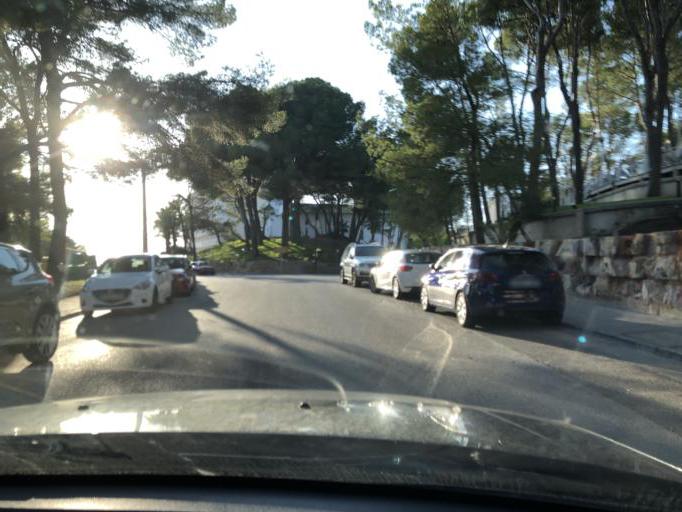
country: ES
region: Balearic Islands
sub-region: Illes Balears
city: Santa Ponsa
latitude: 39.5343
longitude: 2.4606
